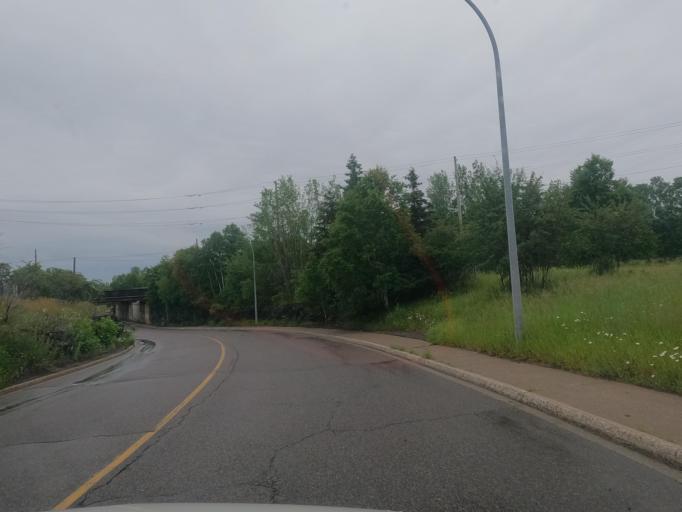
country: CA
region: Ontario
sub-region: Thunder Bay District
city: Thunder Bay
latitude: 48.4547
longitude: -89.1849
